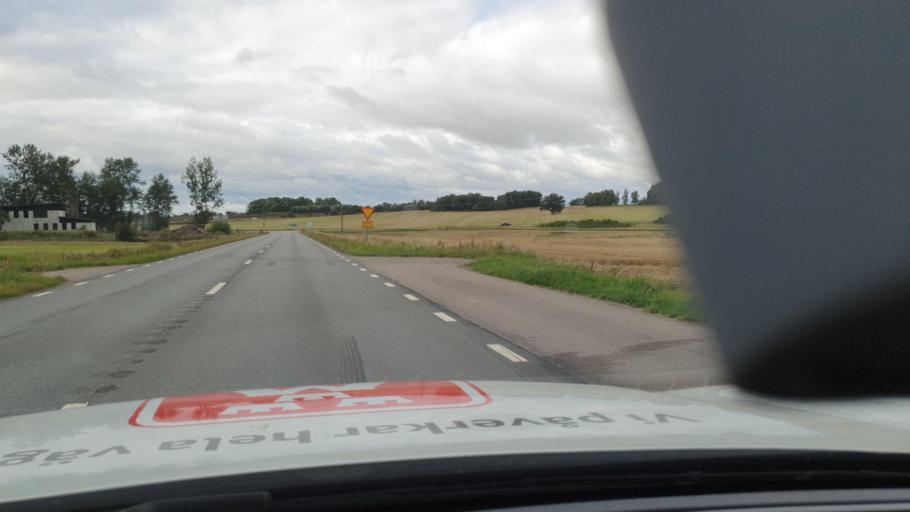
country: SE
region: Skane
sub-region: Helsingborg
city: Hyllinge
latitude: 56.0967
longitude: 12.8020
